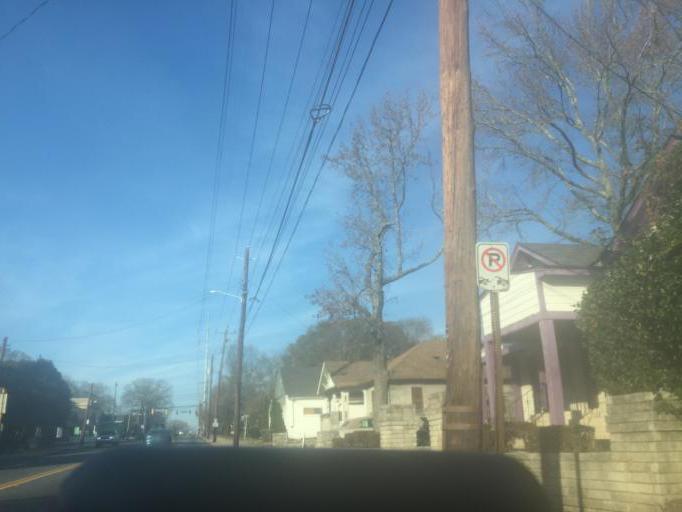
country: US
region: Georgia
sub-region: Fulton County
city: Atlanta
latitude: 33.7299
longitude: -84.4080
